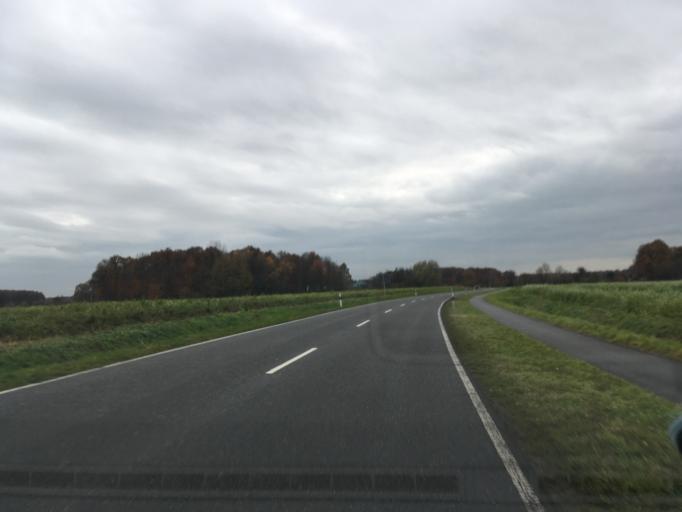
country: DE
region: North Rhine-Westphalia
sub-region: Regierungsbezirk Munster
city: Gescher
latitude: 51.9865
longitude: 7.0312
